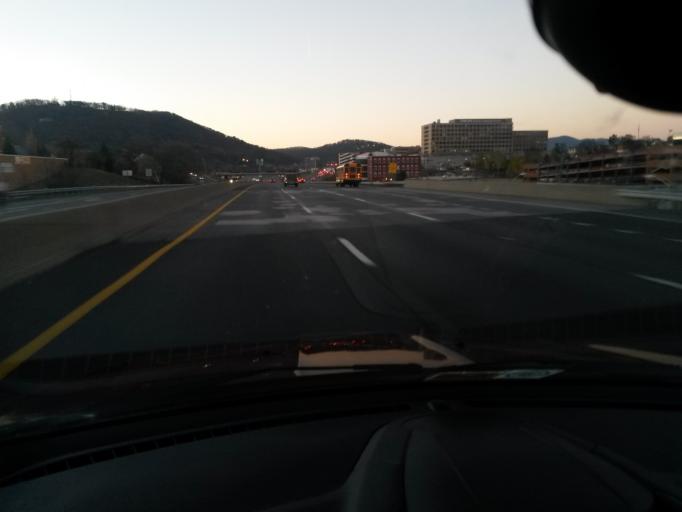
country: US
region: Virginia
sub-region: City of Roanoke
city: Roanoke
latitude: 37.2704
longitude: -79.9364
